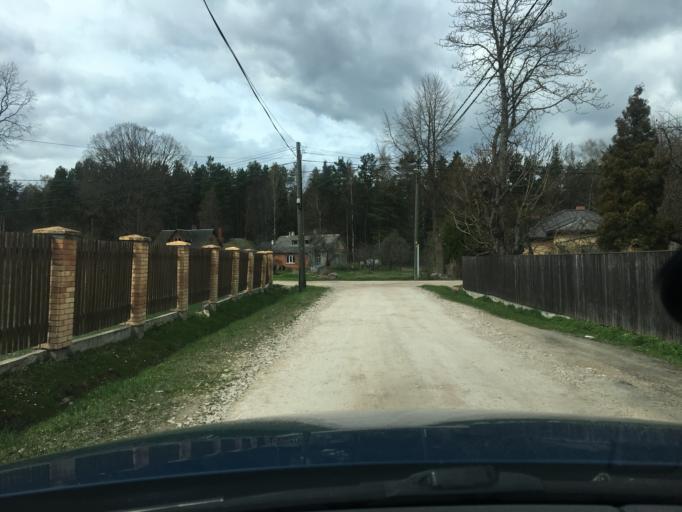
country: LV
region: Engure
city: Smarde
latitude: 56.9492
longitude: 23.4857
